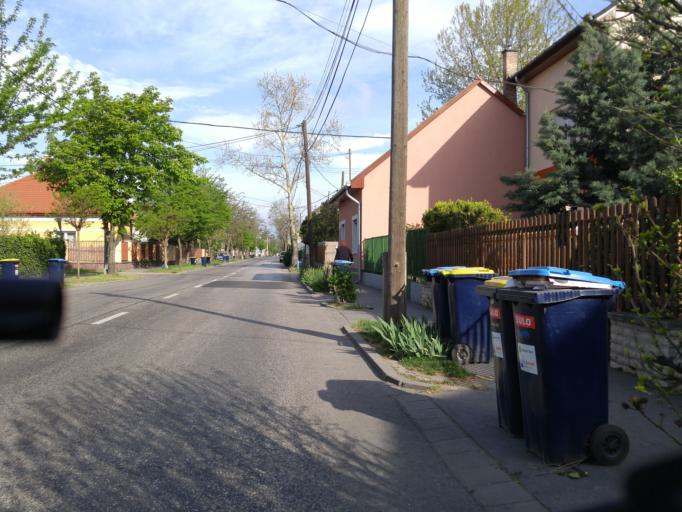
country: HU
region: Budapest
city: Budapest XX. keruelet
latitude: 47.4337
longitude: 19.1268
